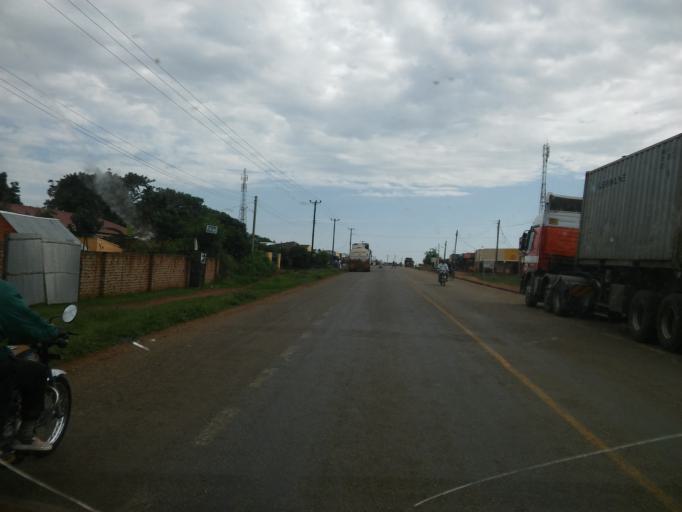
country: UG
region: Eastern Region
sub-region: Mbale District
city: Mbale
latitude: 1.1396
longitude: 34.1648
